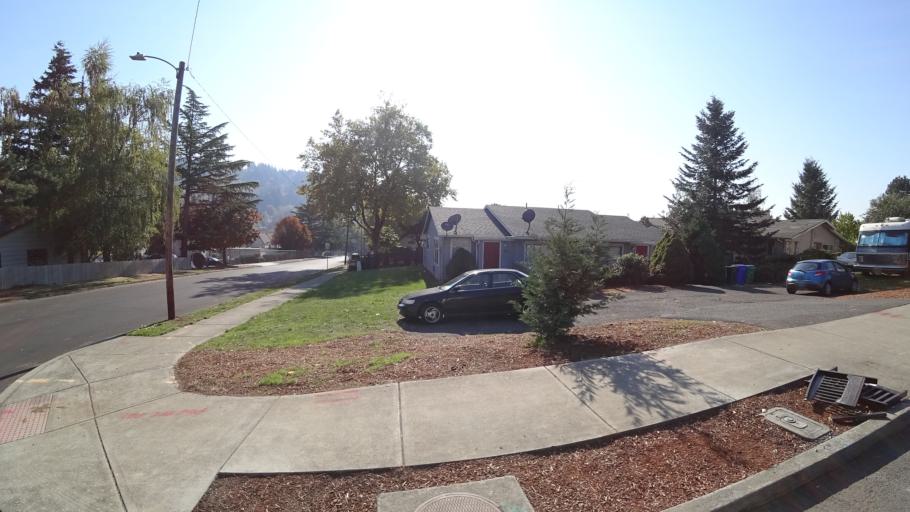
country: US
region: Oregon
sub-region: Multnomah County
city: Gresham
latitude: 45.4971
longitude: -122.4426
